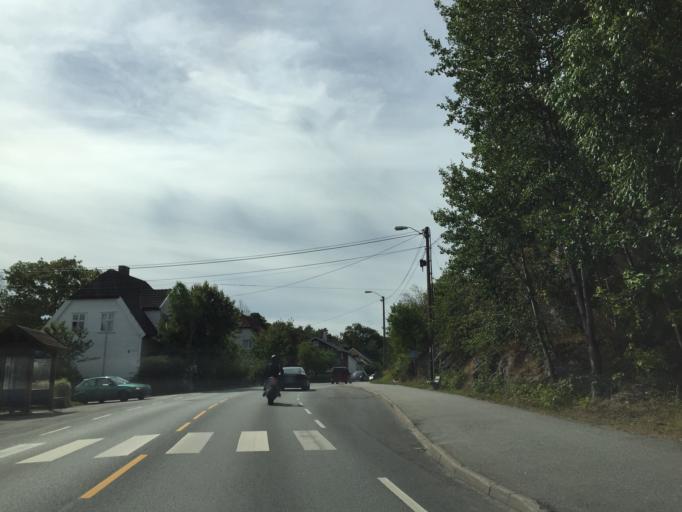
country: NO
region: Ostfold
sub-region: Fredrikstad
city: Fredrikstad
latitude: 59.1955
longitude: 10.9418
